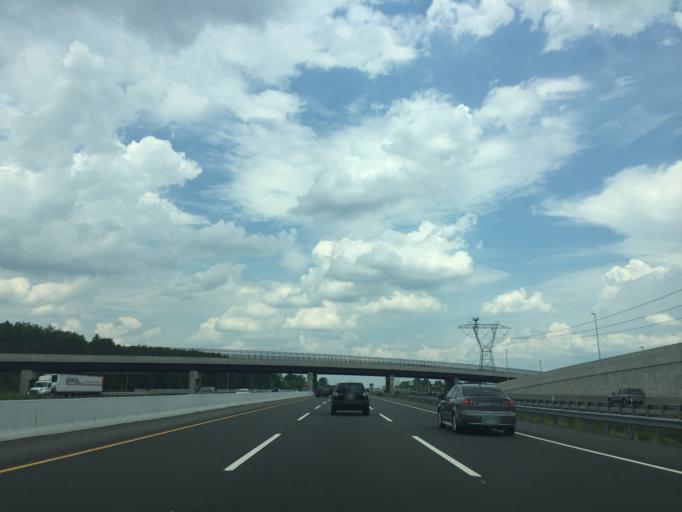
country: US
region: New Jersey
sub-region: Mercer County
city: Yardville
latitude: 40.1706
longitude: -74.6411
